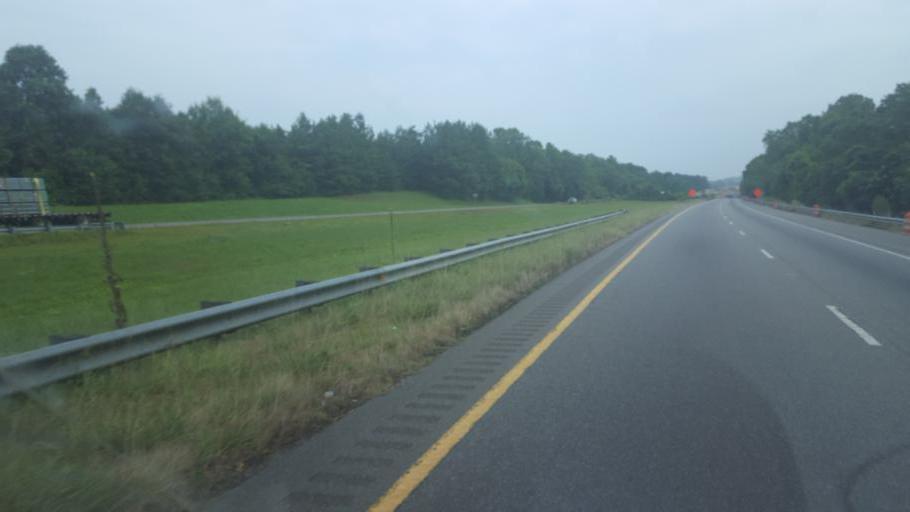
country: US
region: North Carolina
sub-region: Iredell County
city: Statesville
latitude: 35.8876
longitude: -80.8645
